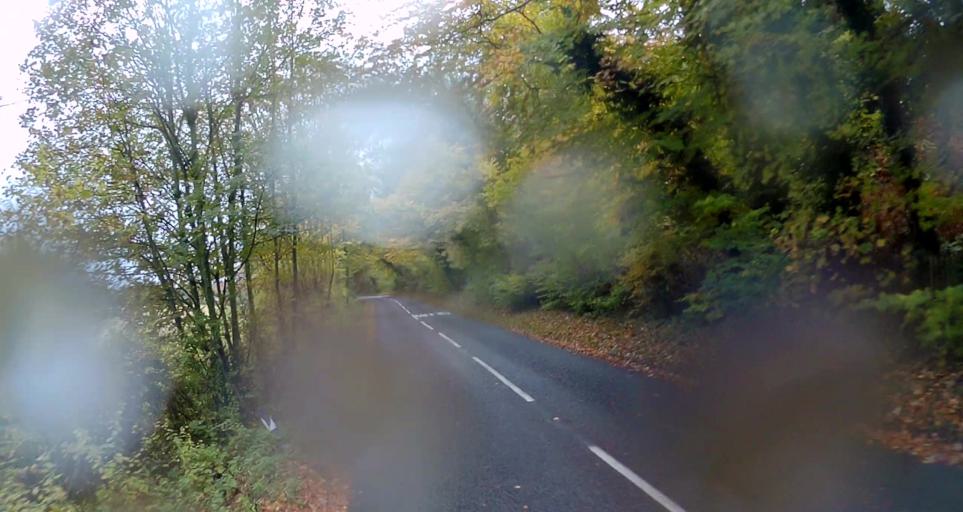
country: GB
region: England
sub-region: Hampshire
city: Kings Worthy
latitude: 51.1252
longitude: -1.1868
